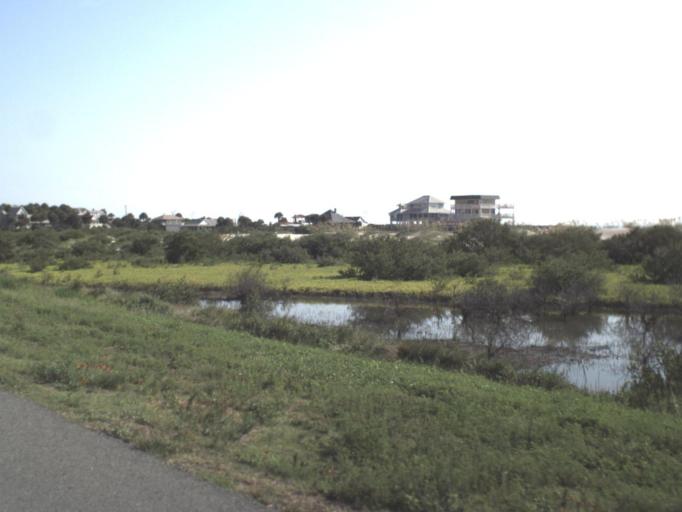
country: US
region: Florida
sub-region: Flagler County
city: Palm Coast
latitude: 29.6939
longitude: -81.2246
